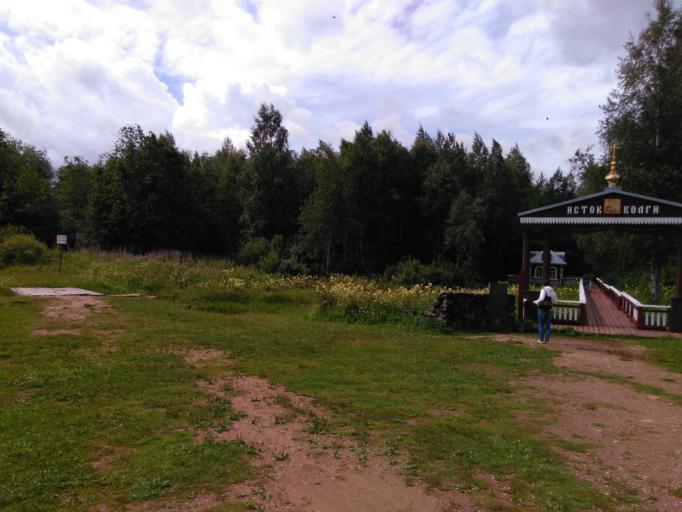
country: RU
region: Novgorod
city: Demyansk
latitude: 57.2516
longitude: 32.4690
